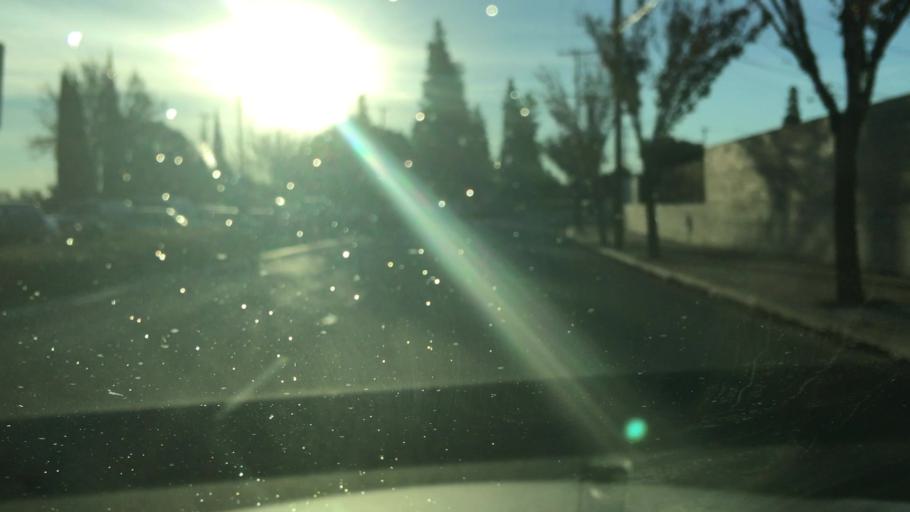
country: US
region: California
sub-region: Los Angeles County
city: East La Mirada
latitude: 33.9294
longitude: -117.9847
